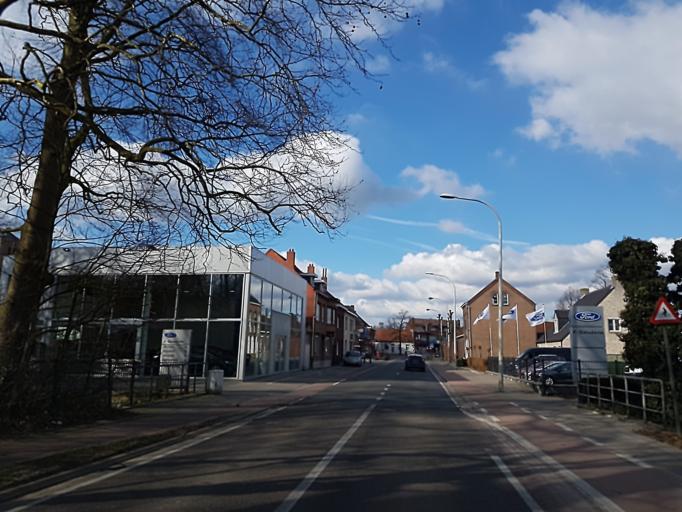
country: BE
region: Flanders
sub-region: Provincie Antwerpen
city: Hoogstraten
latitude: 51.4421
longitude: 4.7389
